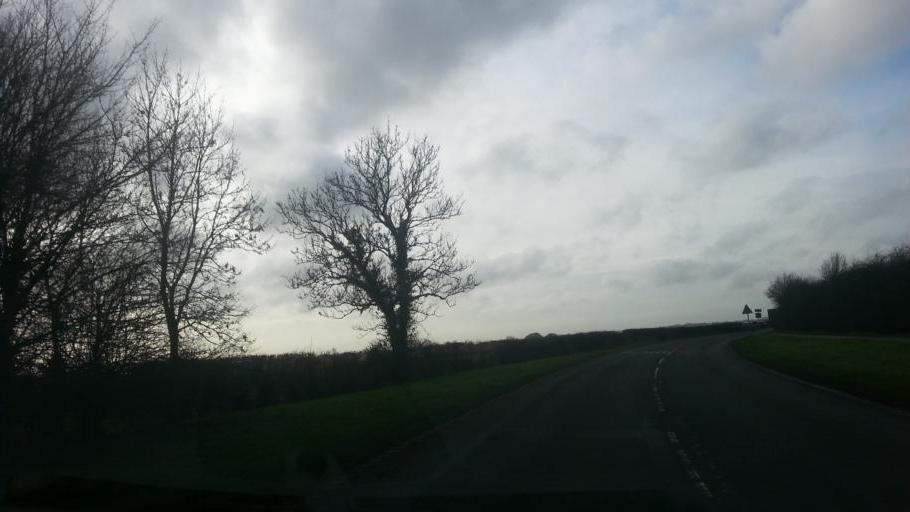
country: GB
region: England
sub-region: District of Rutland
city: Wing
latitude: 52.6349
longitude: -0.6756
